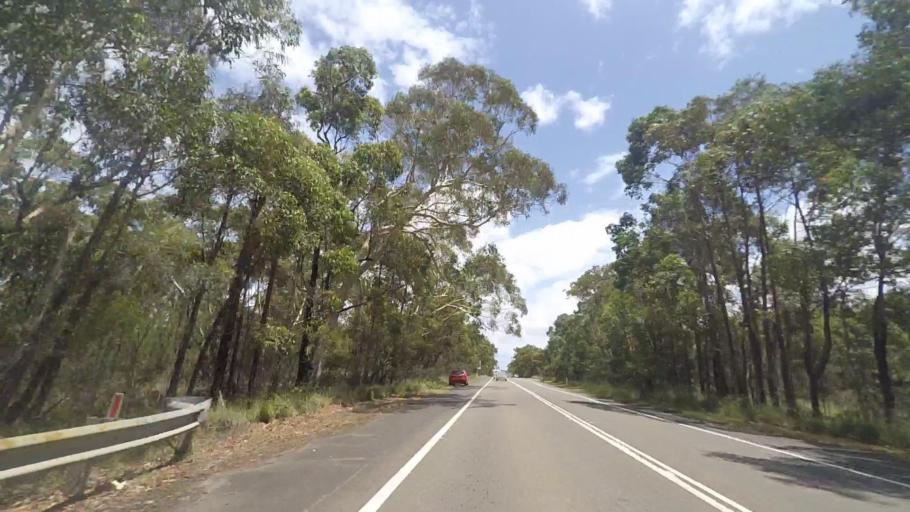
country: AU
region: New South Wales
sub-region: Liverpool
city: East Hills
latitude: -33.9706
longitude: 150.9785
